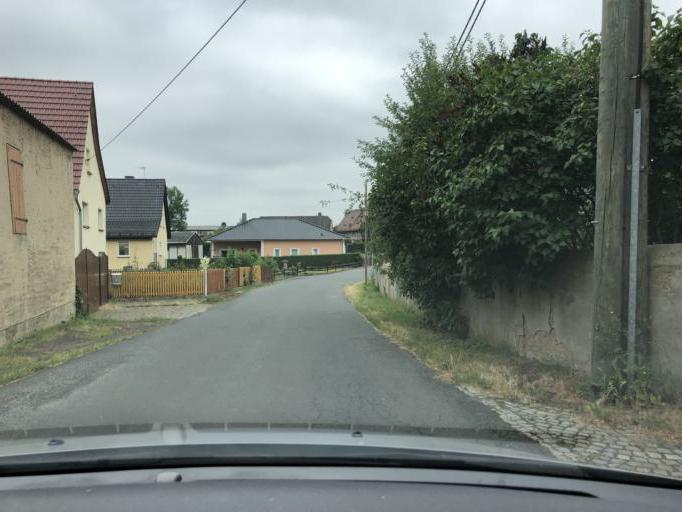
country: DE
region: Saxony
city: Frohburg
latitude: 51.0981
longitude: 12.5596
